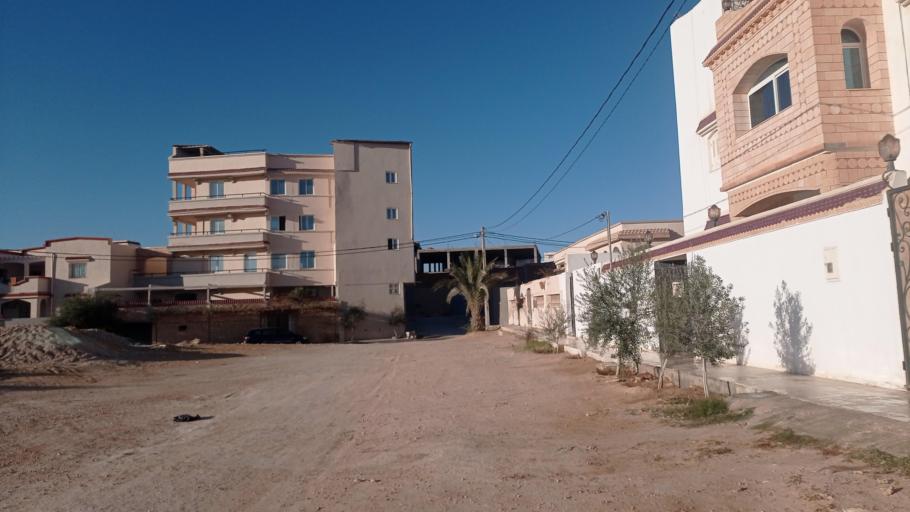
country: TN
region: Qabis
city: Gabes
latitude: 33.8480
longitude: 10.1139
